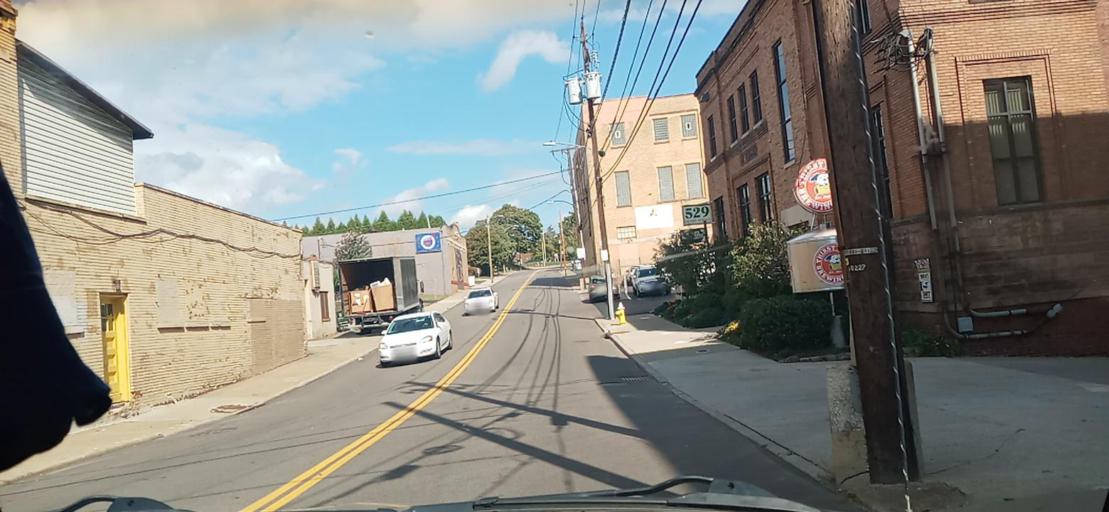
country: US
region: Ohio
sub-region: Summit County
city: Akron
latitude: 41.0687
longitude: -81.5179
